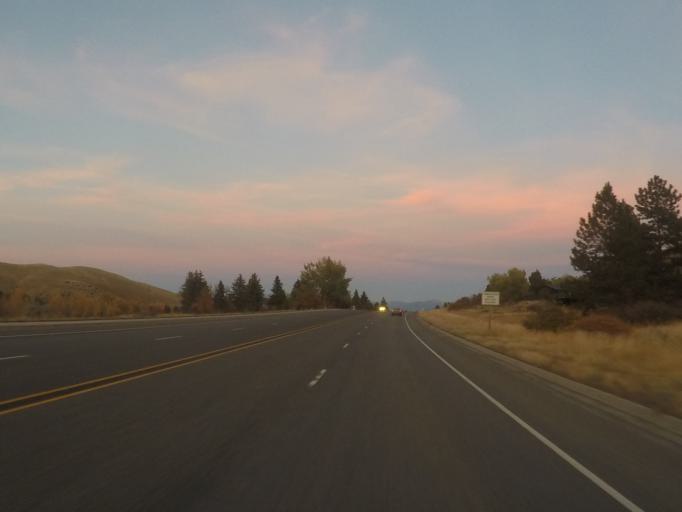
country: US
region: Montana
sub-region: Lewis and Clark County
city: Helena West Side
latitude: 46.5980
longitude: -112.1036
